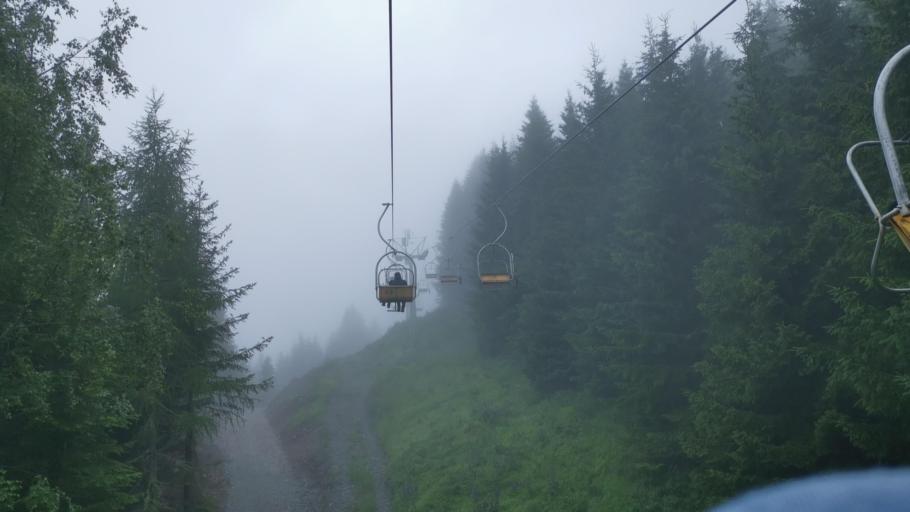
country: AT
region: Tyrol
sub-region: Politischer Bezirk Lienz
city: Leisach
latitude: 46.8195
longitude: 12.7302
